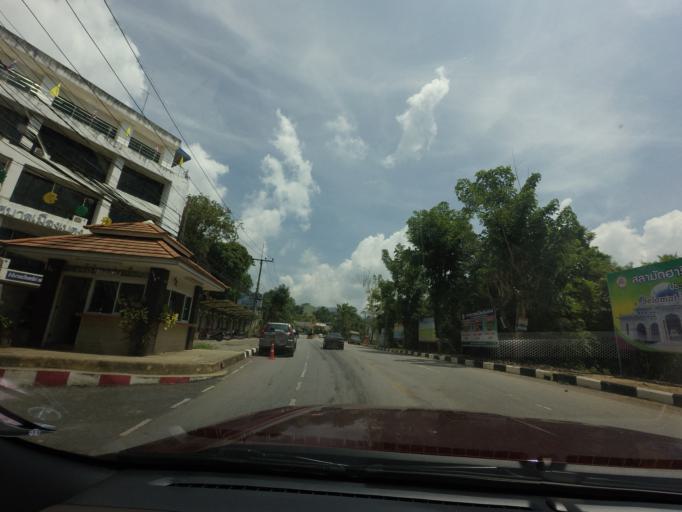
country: TH
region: Yala
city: Betong
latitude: 5.7734
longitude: 101.0648
